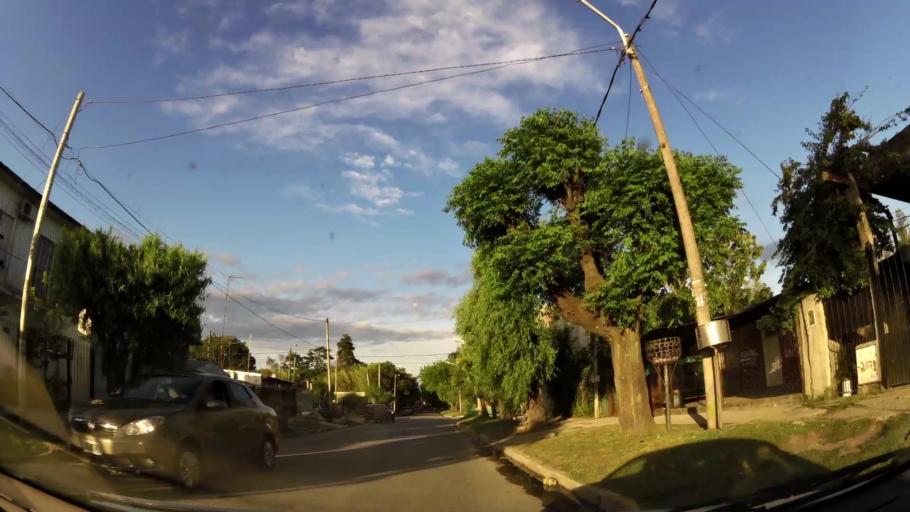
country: AR
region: Buenos Aires
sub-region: Partido de Merlo
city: Merlo
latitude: -34.6820
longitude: -58.7566
